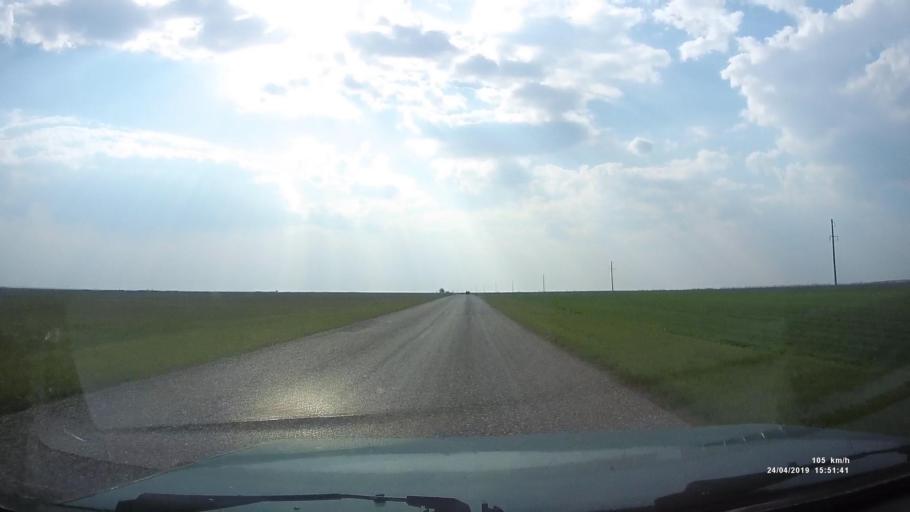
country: RU
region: Kalmykiya
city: Yashalta
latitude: 46.6044
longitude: 42.6050
